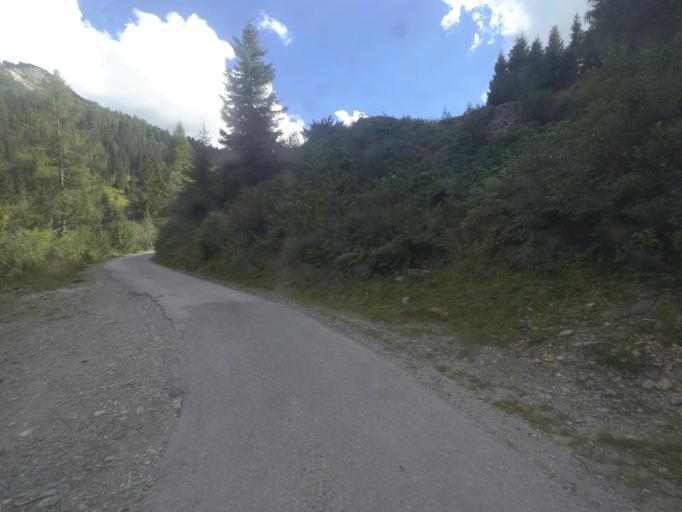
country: AT
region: Salzburg
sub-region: Politischer Bezirk Sankt Johann im Pongau
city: Kleinarl
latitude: 47.1811
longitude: 13.3547
